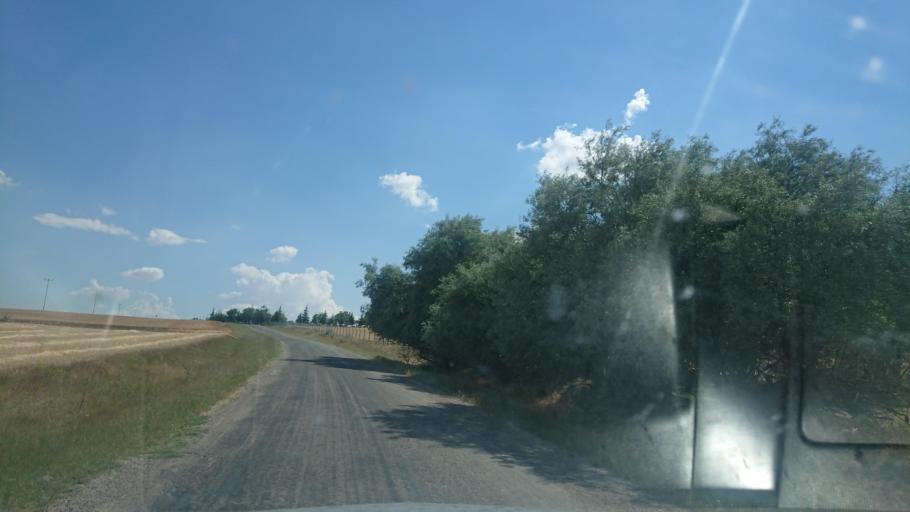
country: TR
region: Aksaray
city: Agacoren
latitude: 38.7653
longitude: 33.7834
